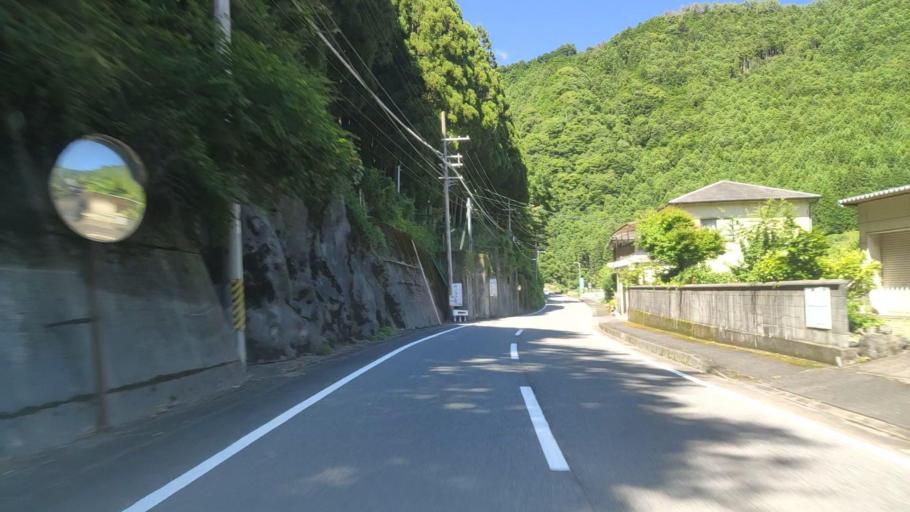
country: JP
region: Nara
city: Yoshino-cho
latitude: 34.2939
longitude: 136.0007
